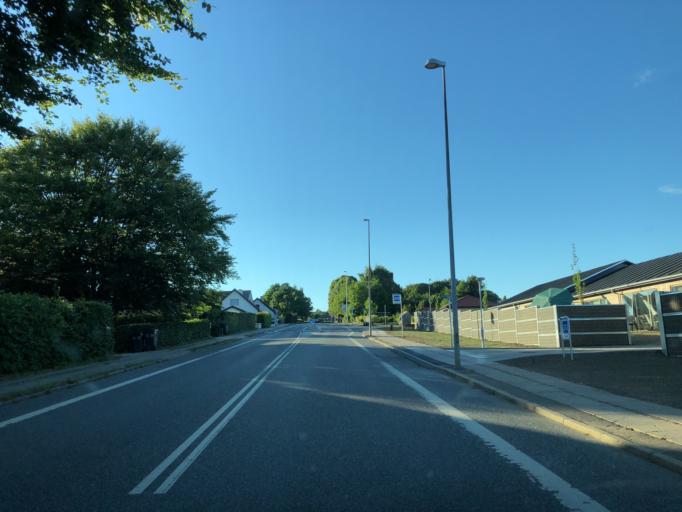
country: DK
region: Central Jutland
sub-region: Horsens Kommune
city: Horsens
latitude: 55.9002
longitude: 9.8379
